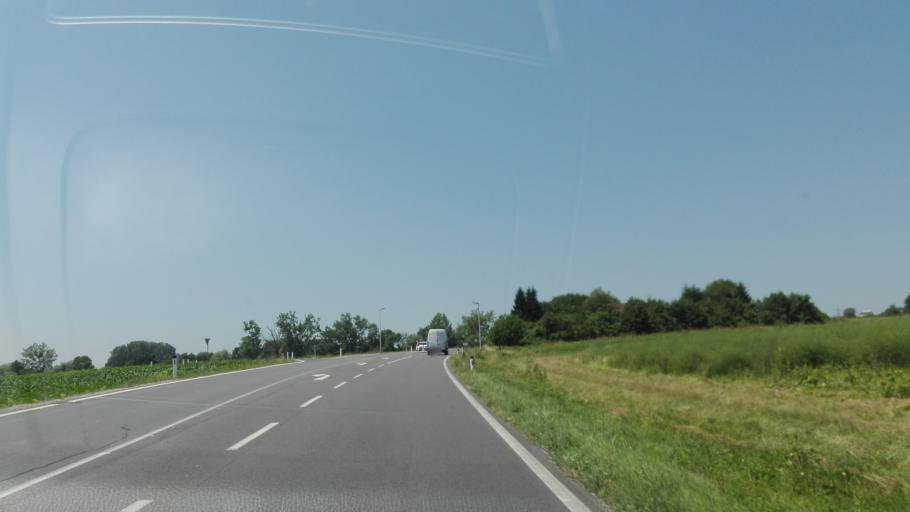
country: AT
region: Upper Austria
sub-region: Politischer Bezirk Linz-Land
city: Pasching
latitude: 48.2690
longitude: 14.2138
